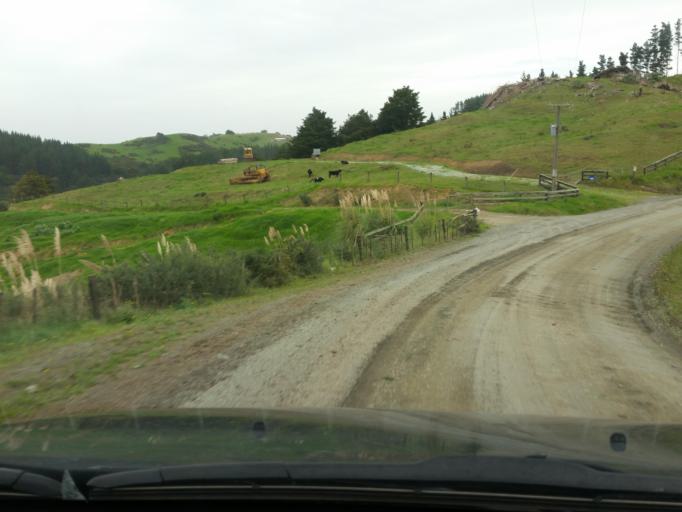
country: NZ
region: Auckland
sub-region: Auckland
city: Wellsford
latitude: -36.1494
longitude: 174.3563
